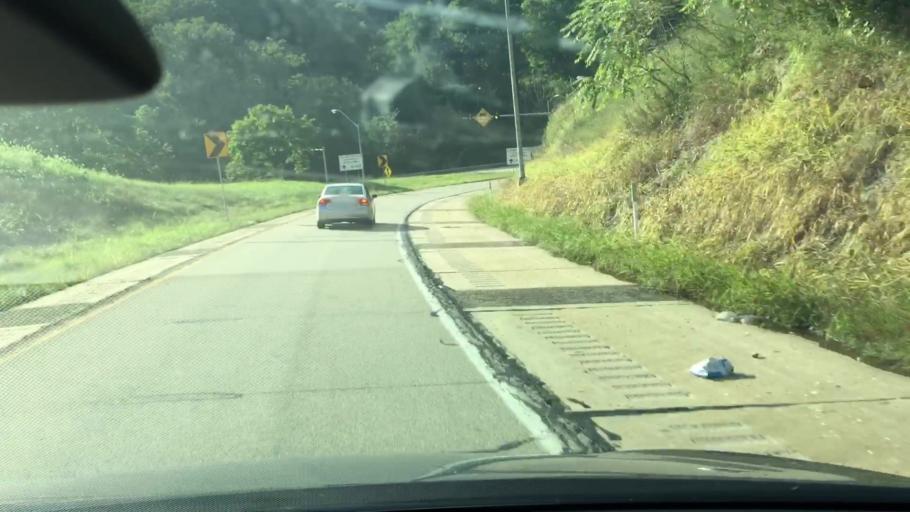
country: US
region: Pennsylvania
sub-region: Allegheny County
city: Churchill
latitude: 40.4424
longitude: -79.8272
